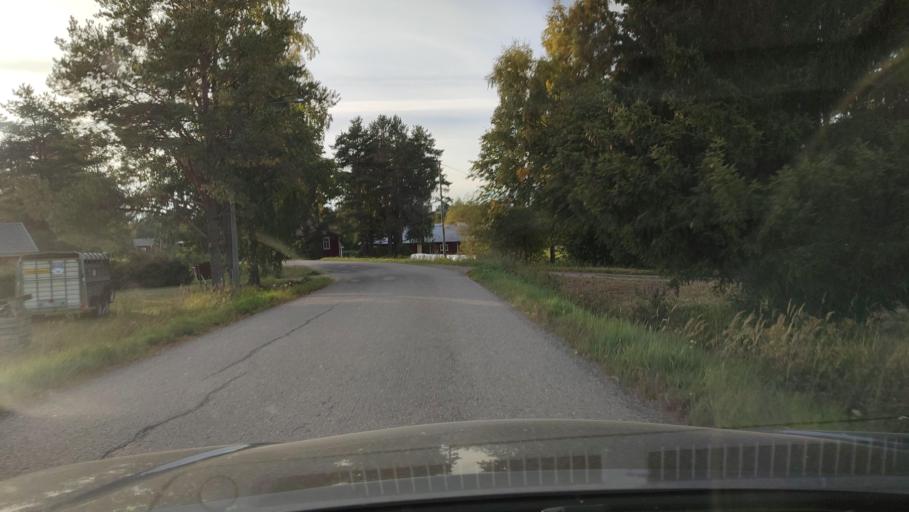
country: FI
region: Southern Ostrobothnia
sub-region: Suupohja
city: Karijoki
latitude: 62.1275
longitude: 21.5899
